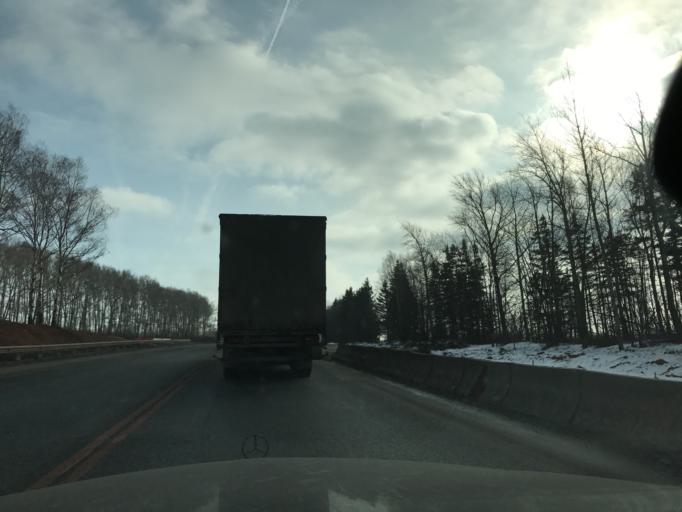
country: RU
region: Vladimir
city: Novovyazniki
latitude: 56.2161
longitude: 42.2476
